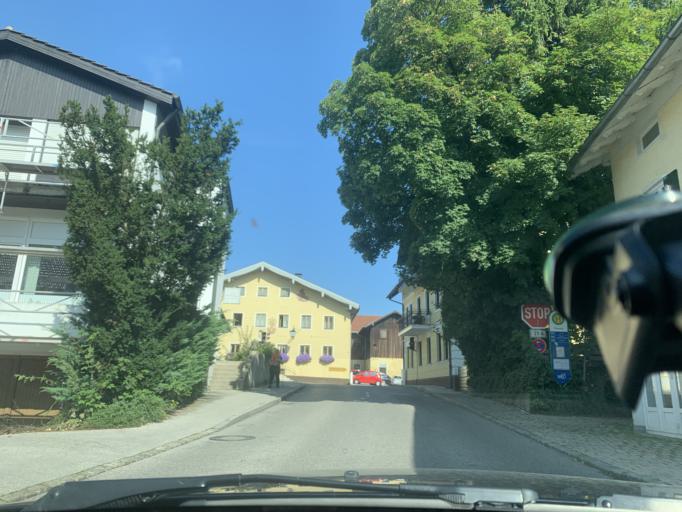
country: DE
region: Bavaria
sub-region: Upper Bavaria
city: Pocking
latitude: 47.9681
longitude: 11.3023
